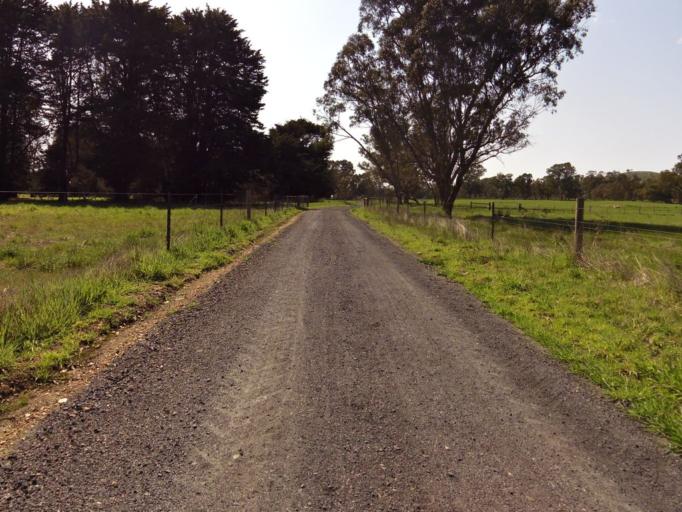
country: AU
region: Victoria
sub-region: Murrindindi
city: Alexandra
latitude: -37.1113
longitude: 145.6100
